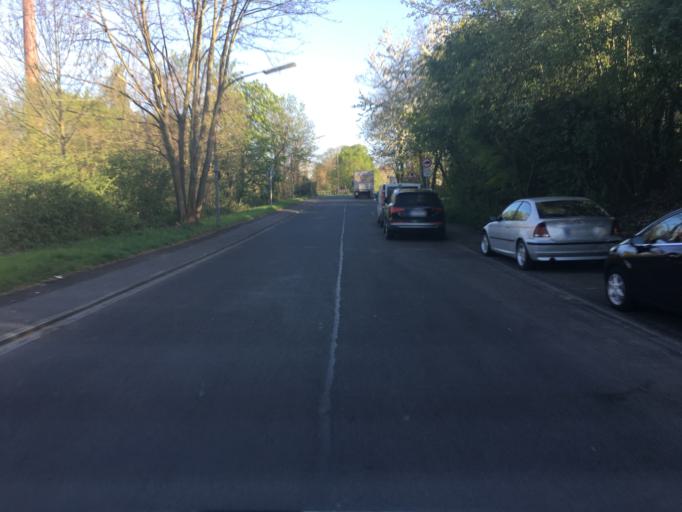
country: DE
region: North Rhine-Westphalia
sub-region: Regierungsbezirk Koln
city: Porz am Rhein
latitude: 50.8782
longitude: 7.0578
